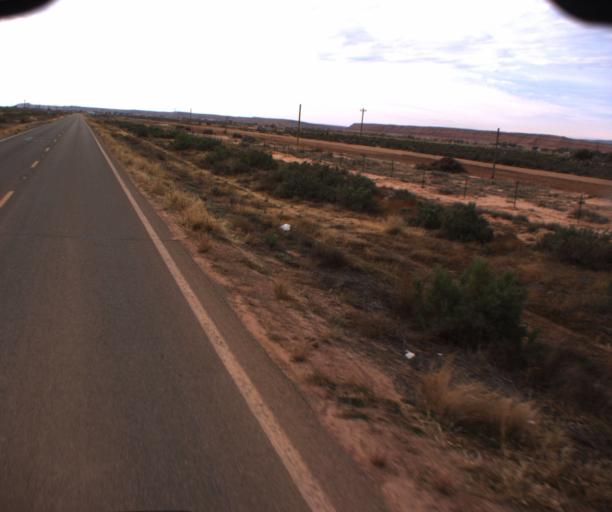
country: US
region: Arizona
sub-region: Apache County
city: Many Farms
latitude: 36.3744
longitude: -109.6126
